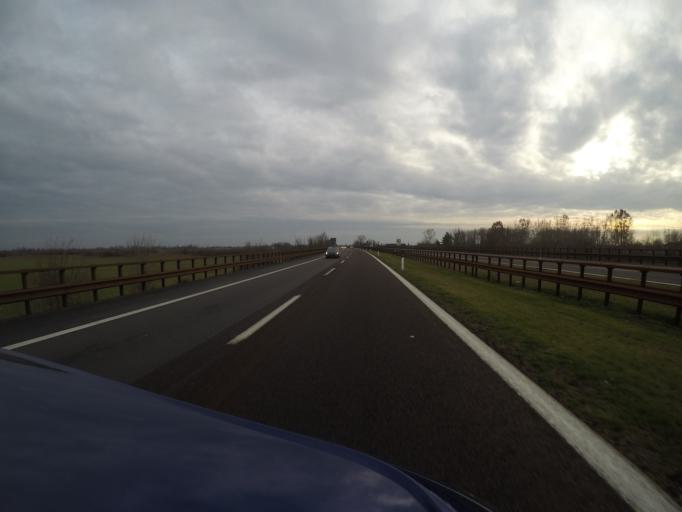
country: IT
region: Emilia-Romagna
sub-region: Provincia di Reggio Emilia
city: Rolo
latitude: 44.9057
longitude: 10.8483
